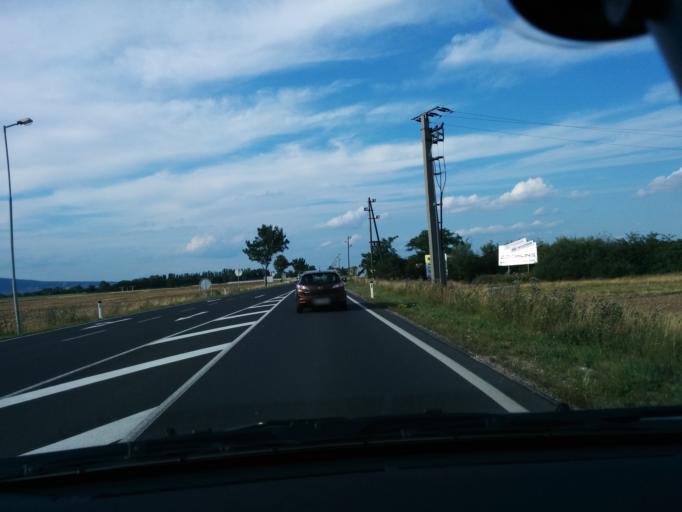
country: AT
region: Lower Austria
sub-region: Politischer Bezirk Baden
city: Gunselsdorf
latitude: 47.9563
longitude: 16.2682
